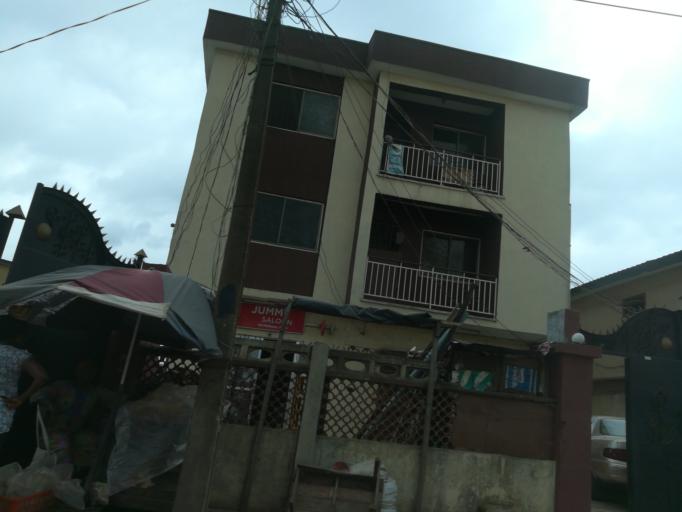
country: NG
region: Lagos
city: Oshodi
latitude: 6.5558
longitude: 3.3338
